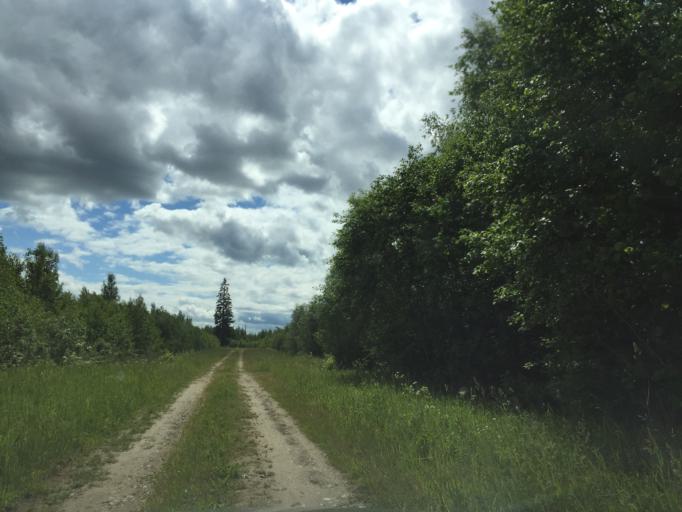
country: LV
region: Lecava
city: Iecava
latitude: 56.5578
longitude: 24.3431
